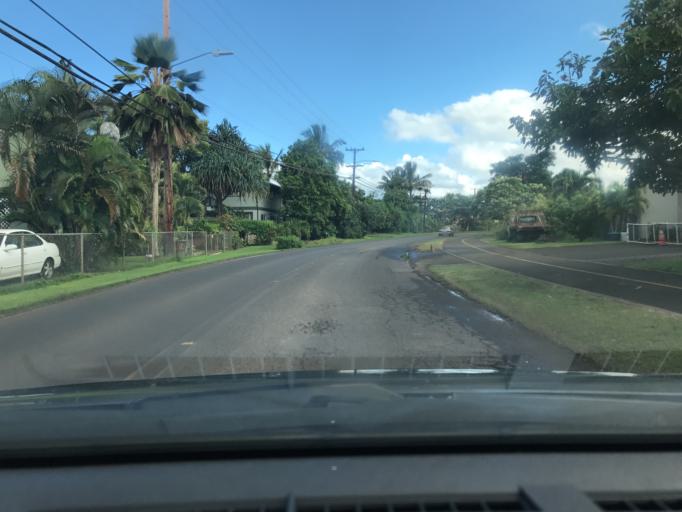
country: US
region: Hawaii
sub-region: Honolulu County
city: Waialua
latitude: 21.5811
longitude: -158.1266
